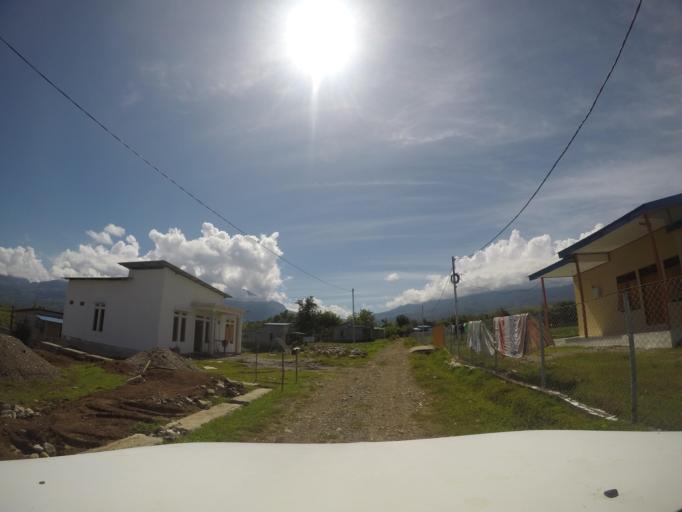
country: TL
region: Bobonaro
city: Maliana
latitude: -8.9860
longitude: 125.1978
